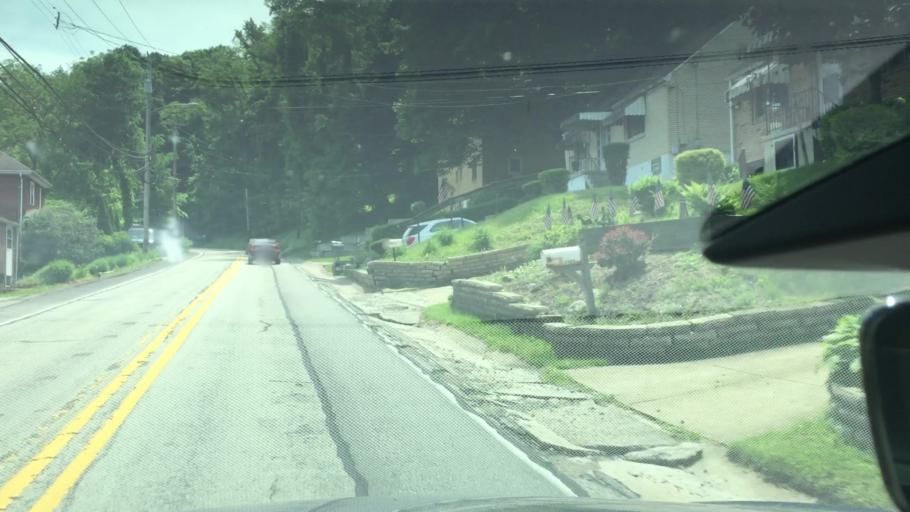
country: US
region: Pennsylvania
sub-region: Allegheny County
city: Blawnox
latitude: 40.4779
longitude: -79.8448
